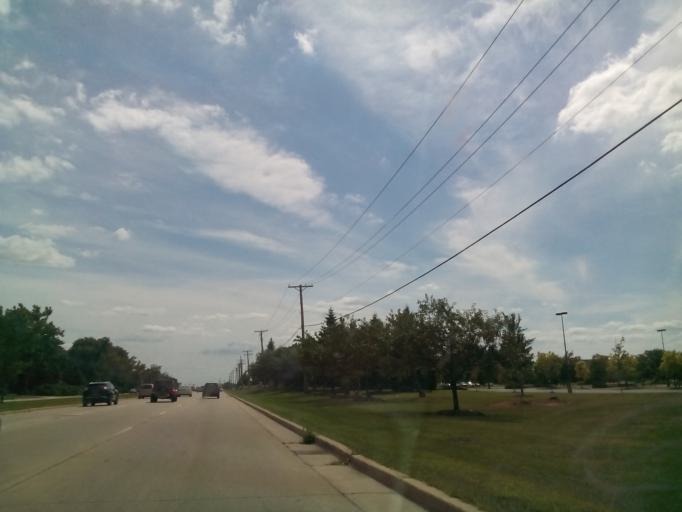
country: US
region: Illinois
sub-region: DuPage County
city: Naperville
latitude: 41.7381
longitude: -88.2063
